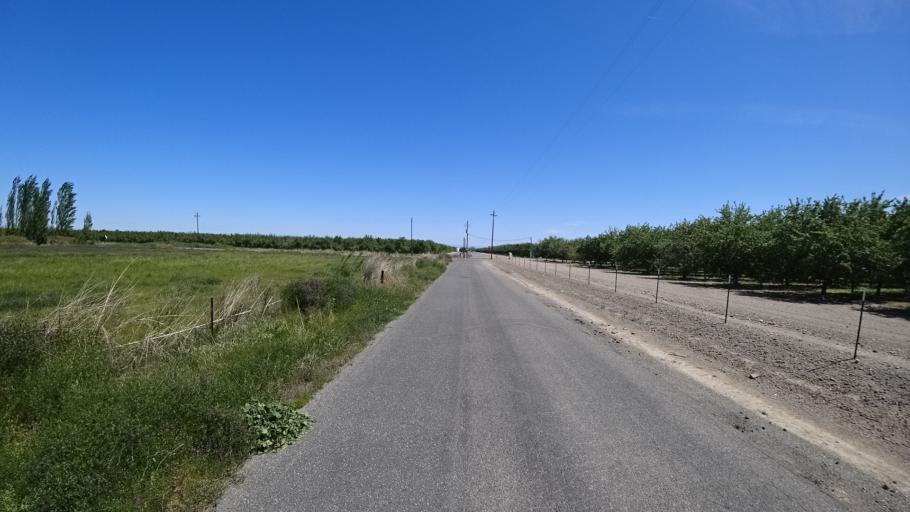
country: US
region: California
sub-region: Glenn County
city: Orland
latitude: 39.7324
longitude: -122.1420
